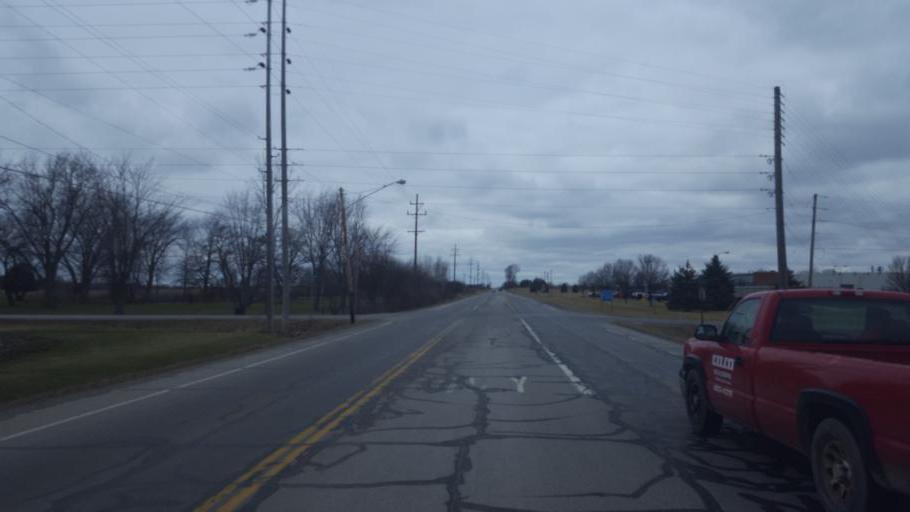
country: US
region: Ohio
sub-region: Crawford County
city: Crestline
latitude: 40.7863
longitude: -82.6969
